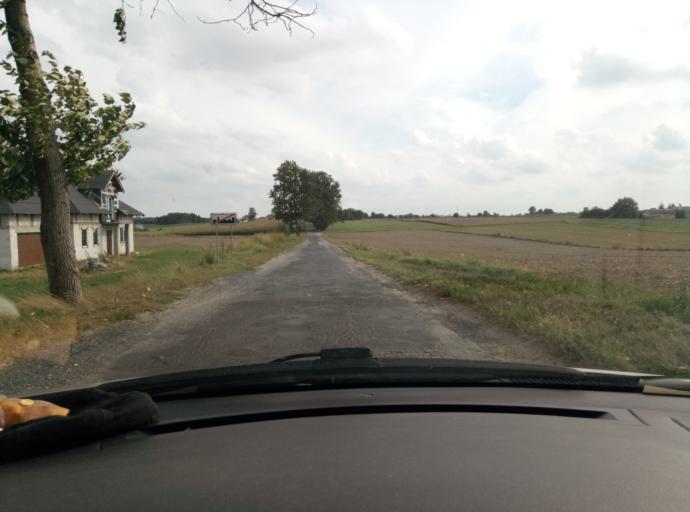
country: PL
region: Kujawsko-Pomorskie
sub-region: Powiat brodnicki
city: Jablonowo Pomorskie
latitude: 53.3846
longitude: 19.2456
